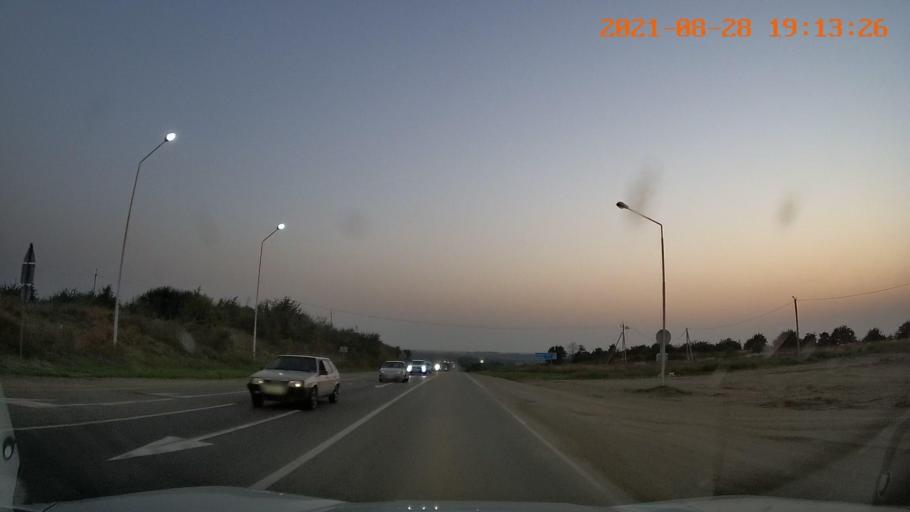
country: RU
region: Krasnodarskiy
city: Ryazanskaya
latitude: 44.9400
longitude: 39.5971
